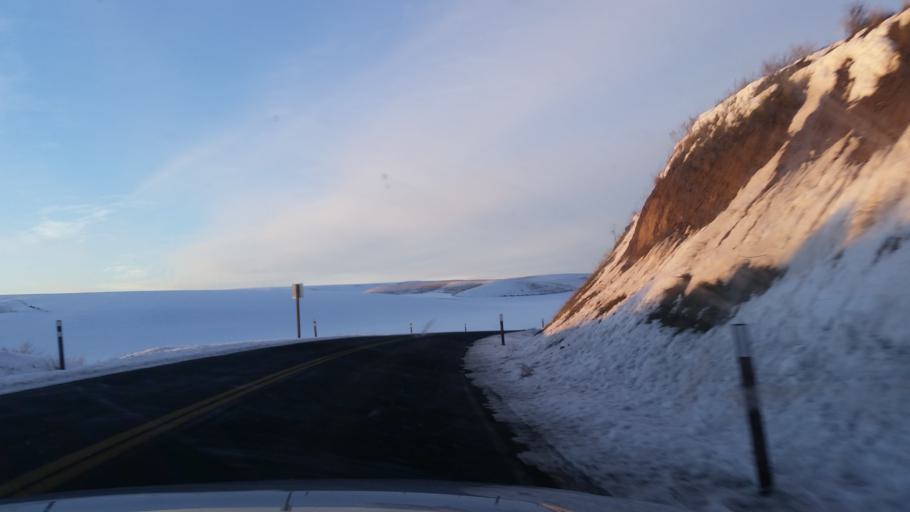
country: US
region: Washington
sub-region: Spokane County
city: Cheney
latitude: 47.1427
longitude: -117.8331
